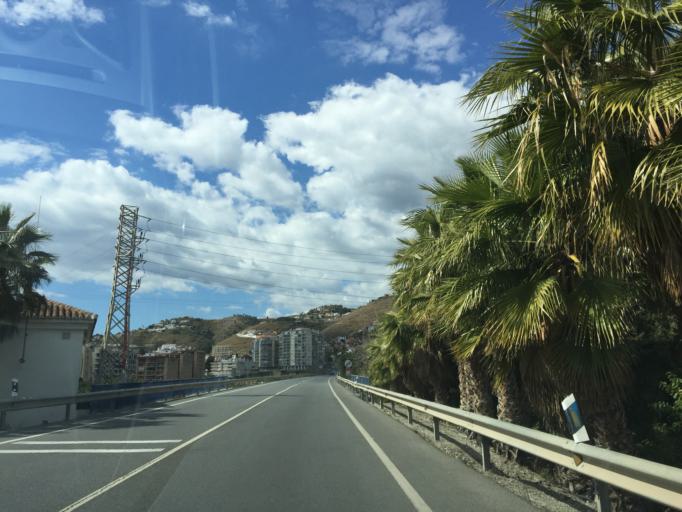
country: ES
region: Andalusia
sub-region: Provincia de Granada
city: Almunecar
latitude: 36.7377
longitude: -3.6909
